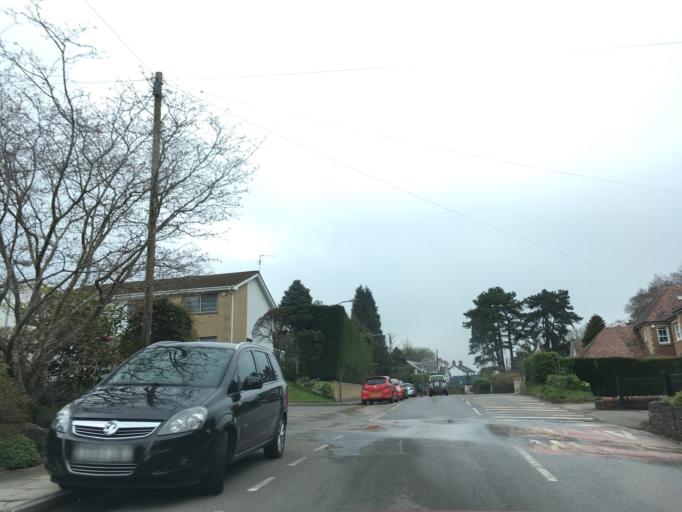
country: GB
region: Wales
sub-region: Cardiff
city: Cardiff
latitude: 51.5387
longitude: -3.1692
